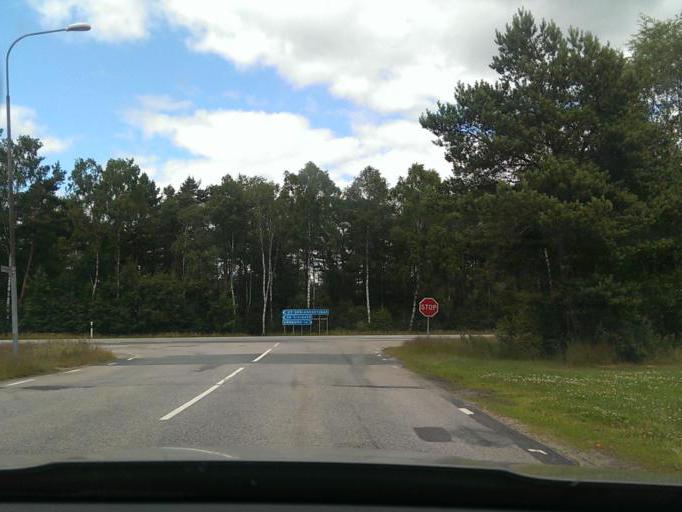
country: SE
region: Joenkoeping
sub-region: Varnamo Kommun
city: Forsheda
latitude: 57.1669
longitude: 13.8284
